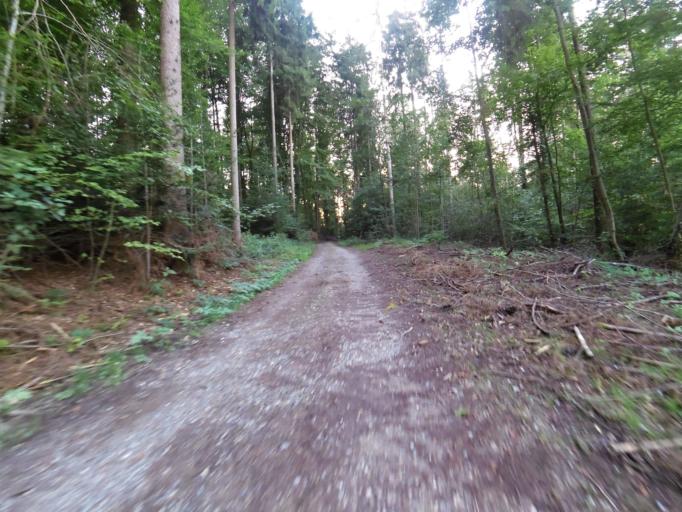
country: CH
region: Thurgau
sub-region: Weinfelden District
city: Wigoltingen
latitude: 47.5771
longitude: 9.0149
